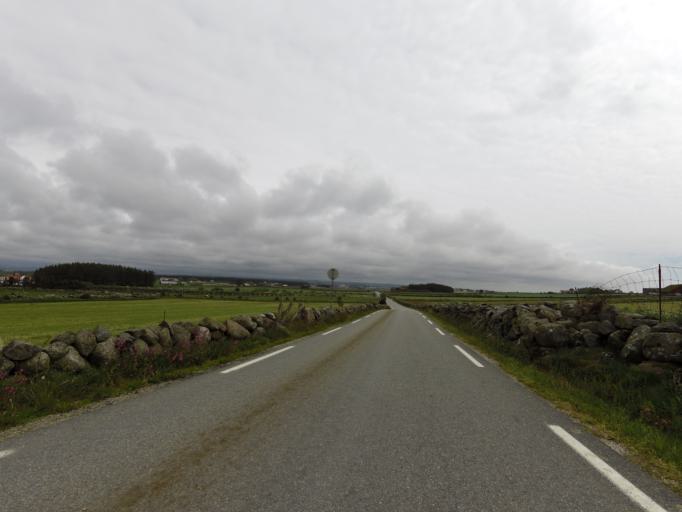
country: NO
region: Rogaland
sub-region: Ha
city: Naerbo
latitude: 58.6574
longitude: 5.5674
